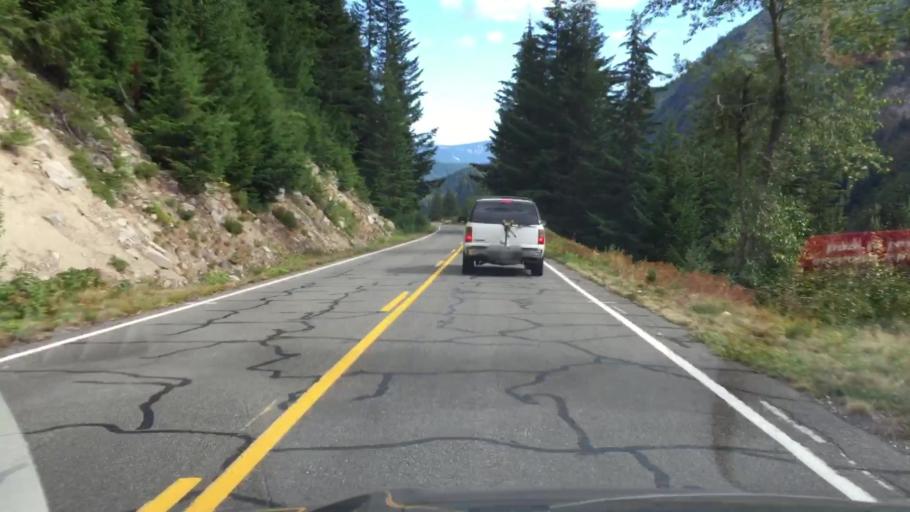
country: US
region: Washington
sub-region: Pierce County
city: Buckley
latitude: 46.7730
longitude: -121.6946
